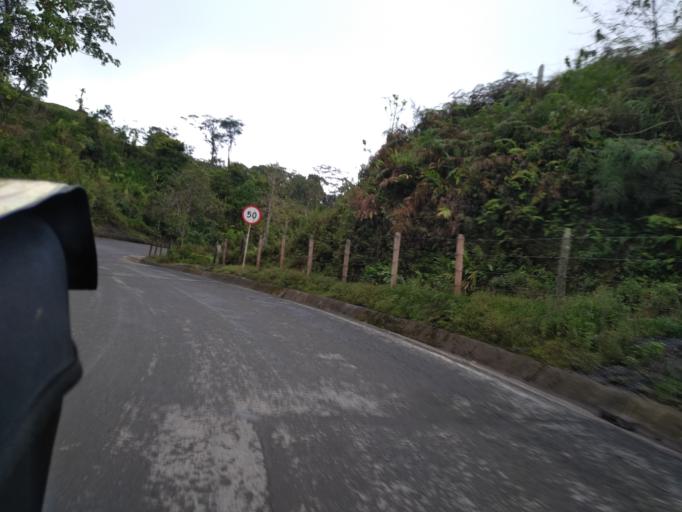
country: CO
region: Santander
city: Landazuri
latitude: 6.1865
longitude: -73.7187
